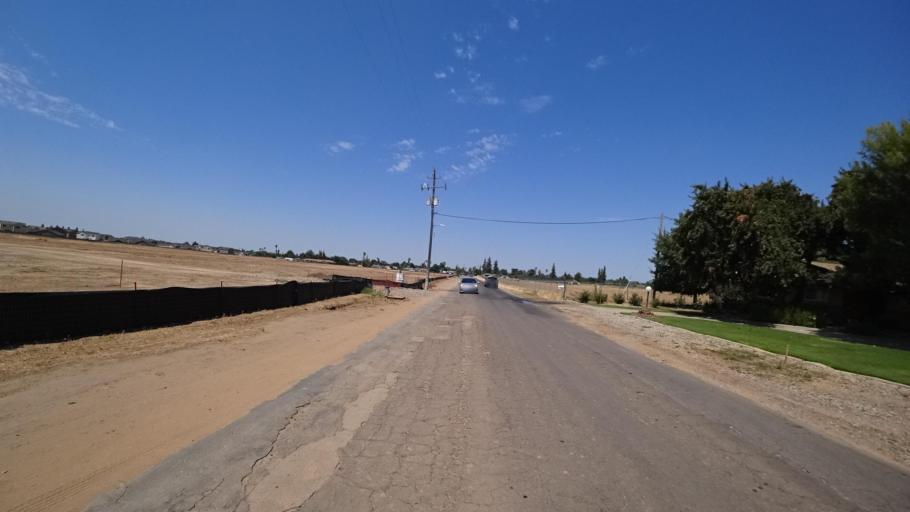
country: US
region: California
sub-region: Fresno County
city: Tarpey Village
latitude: 36.7866
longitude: -119.6774
